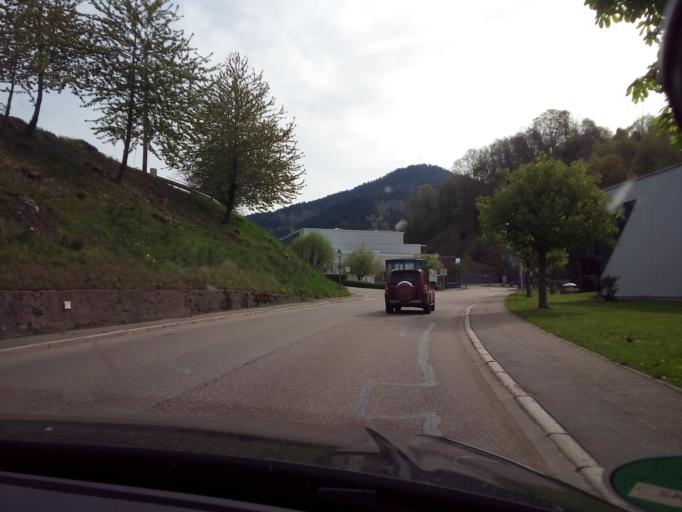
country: DE
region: Baden-Wuerttemberg
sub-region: Freiburg Region
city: Bad Peterstal-Griesbach
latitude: 48.4274
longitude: 8.1989
